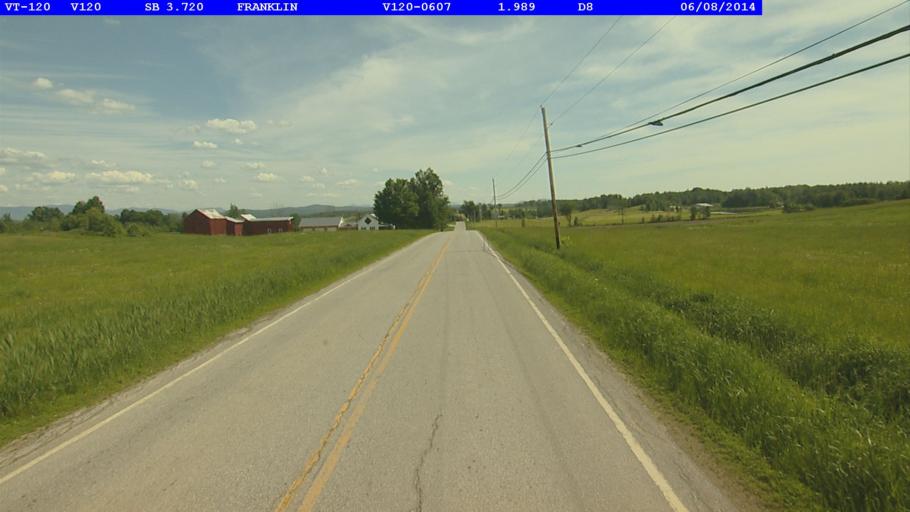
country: US
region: Vermont
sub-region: Franklin County
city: Enosburg Falls
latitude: 44.9617
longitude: -72.9068
